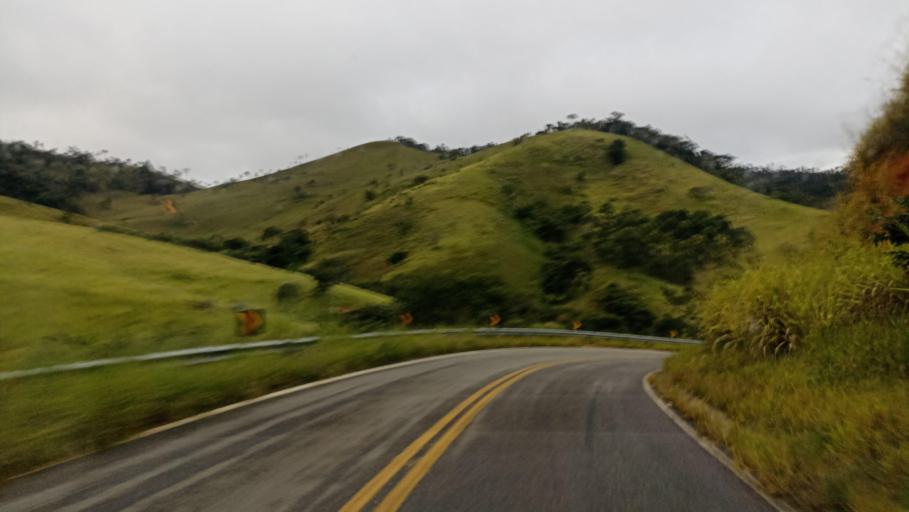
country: BR
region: Bahia
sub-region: Itanhem
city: Itanhem
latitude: -16.6905
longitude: -40.5106
